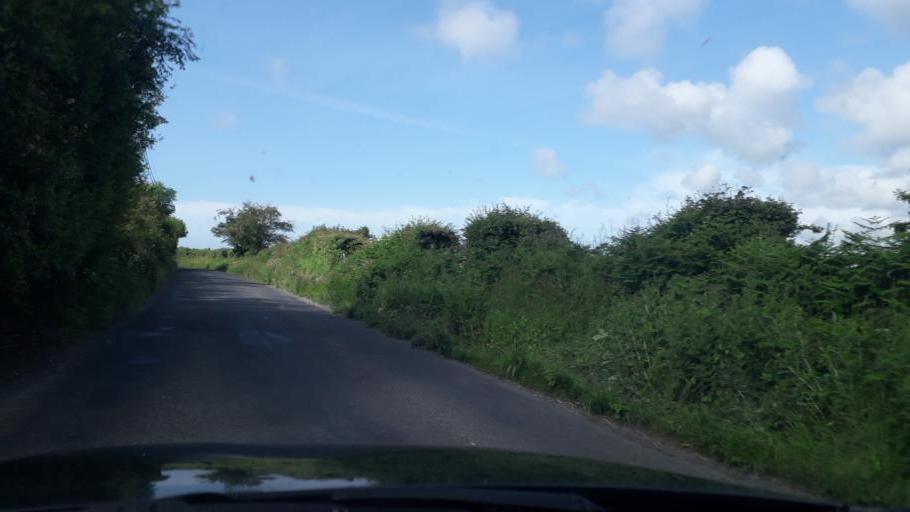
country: IE
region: Leinster
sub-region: Loch Garman
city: Loch Garman
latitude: 52.2391
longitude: -6.5516
